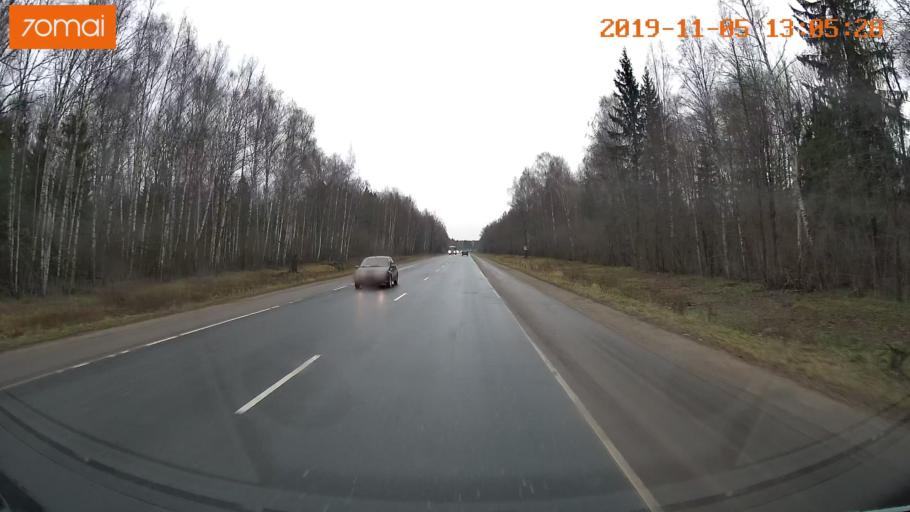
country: RU
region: Ivanovo
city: Kitovo
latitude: 56.8824
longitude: 41.2434
